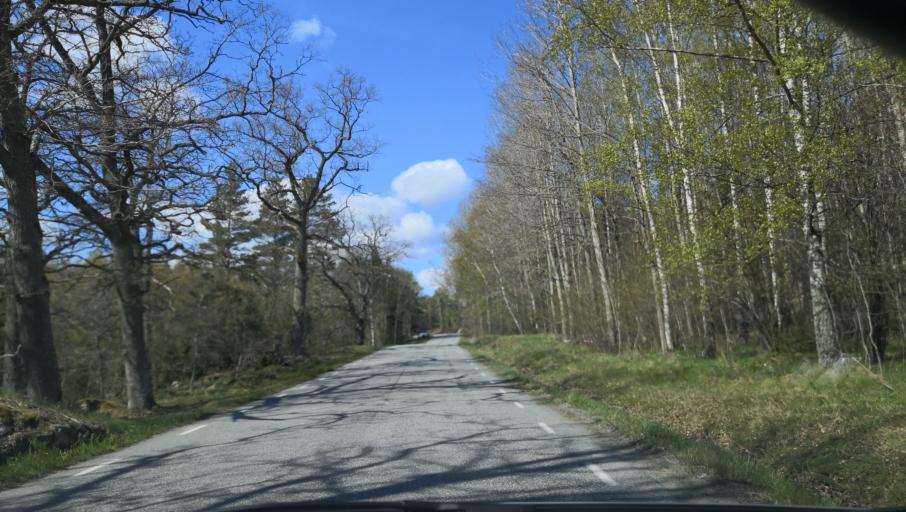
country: SE
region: Stockholm
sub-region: Varmdo Kommun
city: Hemmesta
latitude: 59.3945
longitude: 18.5121
